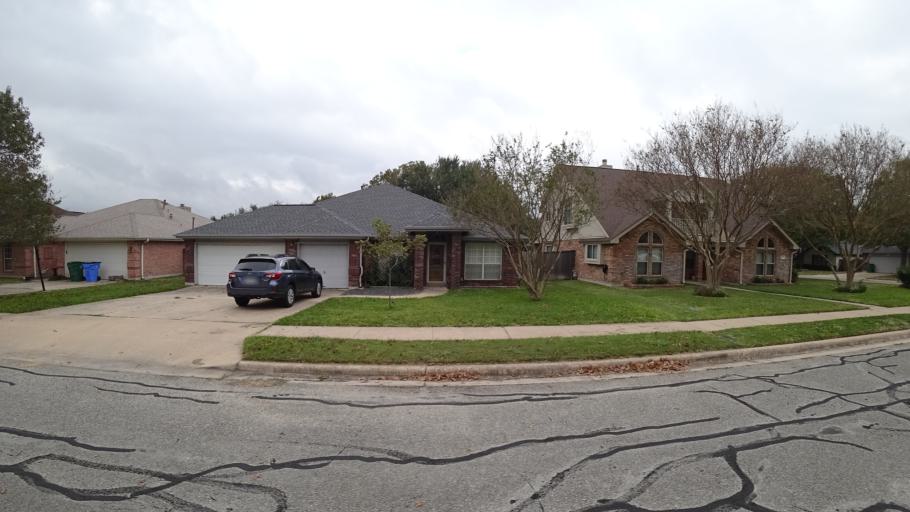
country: US
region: Texas
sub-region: Travis County
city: Pflugerville
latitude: 30.4456
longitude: -97.6113
